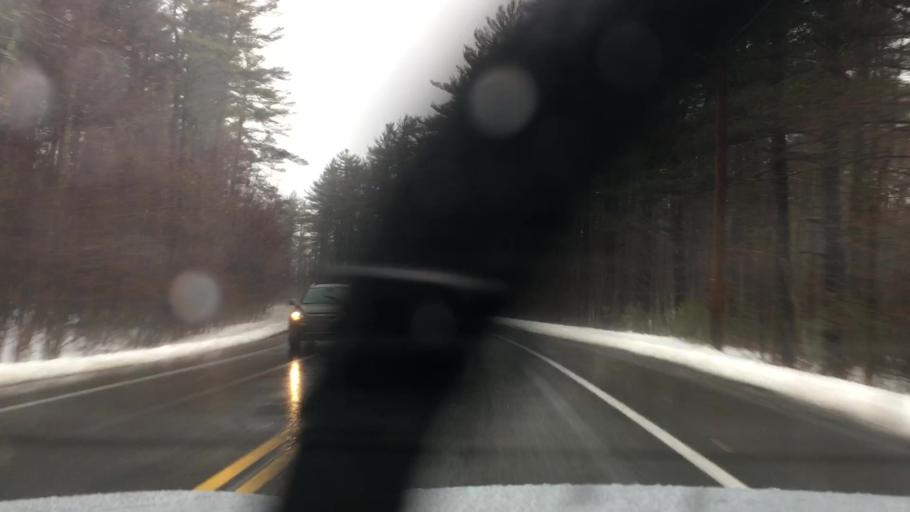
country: US
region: Massachusetts
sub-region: Franklin County
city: Wendell
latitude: 42.5060
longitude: -72.3297
